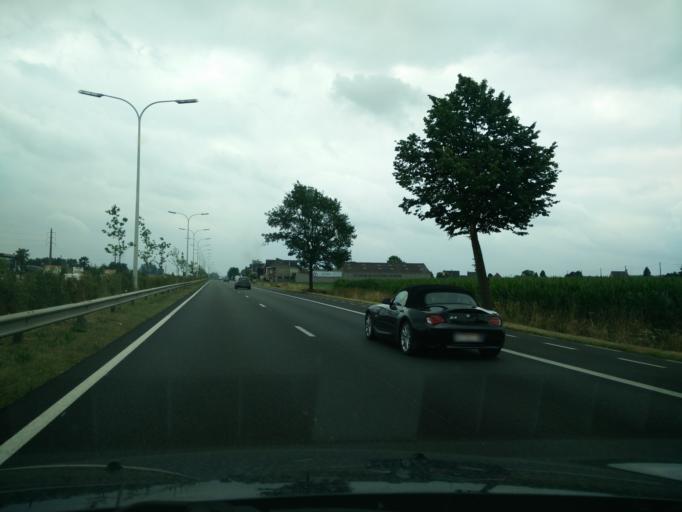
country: BE
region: Flanders
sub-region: Provincie Oost-Vlaanderen
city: Zingem
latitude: 50.8927
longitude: 3.6157
